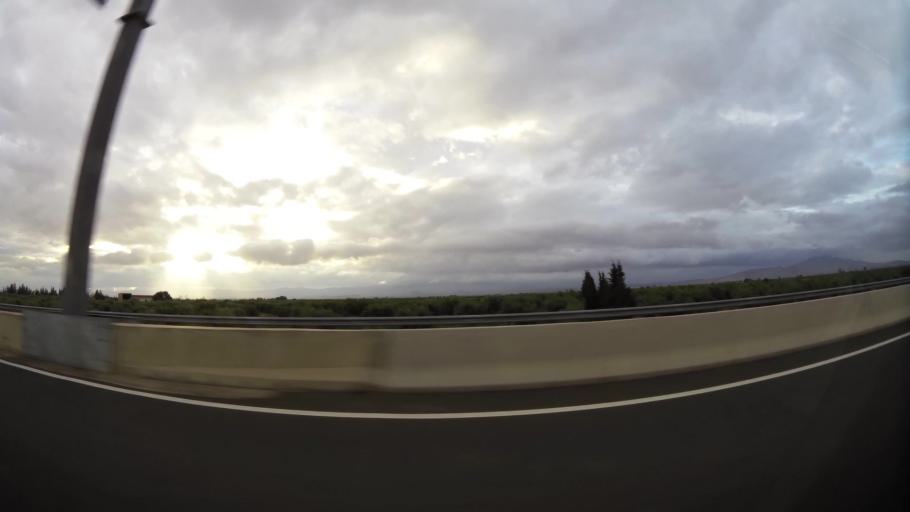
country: MA
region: Taza-Al Hoceima-Taounate
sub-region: Taza
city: Guercif
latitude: 34.3459
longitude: -3.3196
